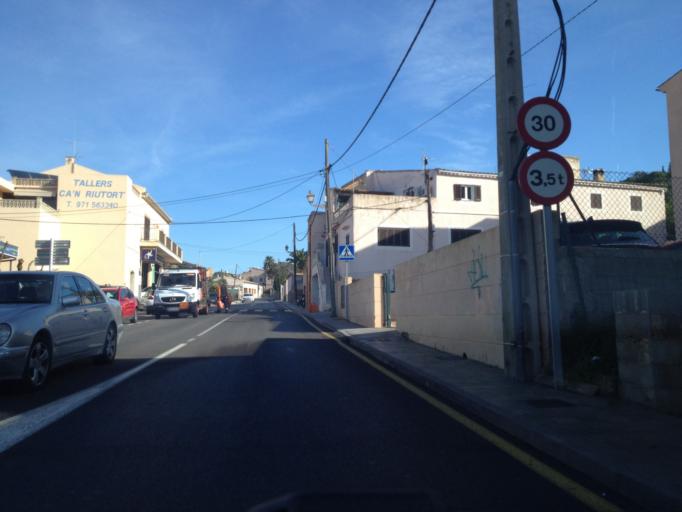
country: ES
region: Balearic Islands
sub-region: Illes Balears
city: Capdepera
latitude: 39.6995
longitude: 3.4285
